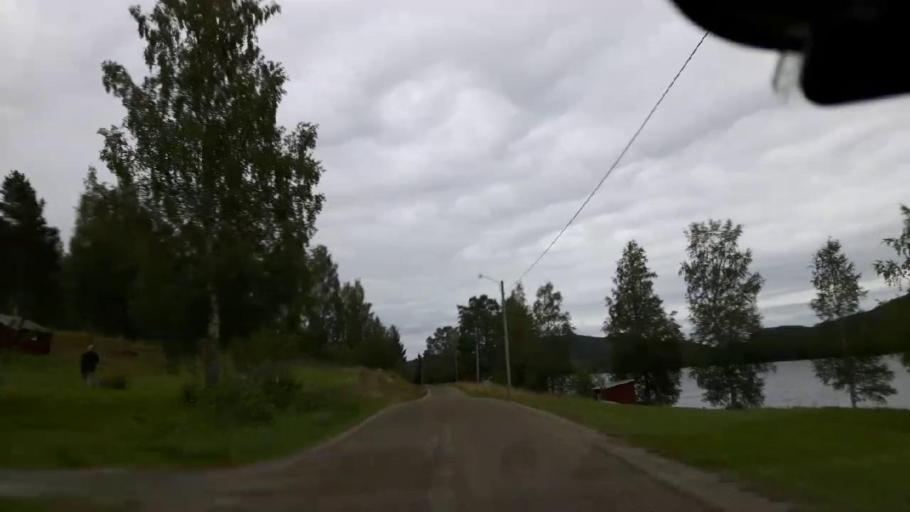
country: SE
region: Jaemtland
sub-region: Braecke Kommun
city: Braecke
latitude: 62.9999
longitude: 15.3813
